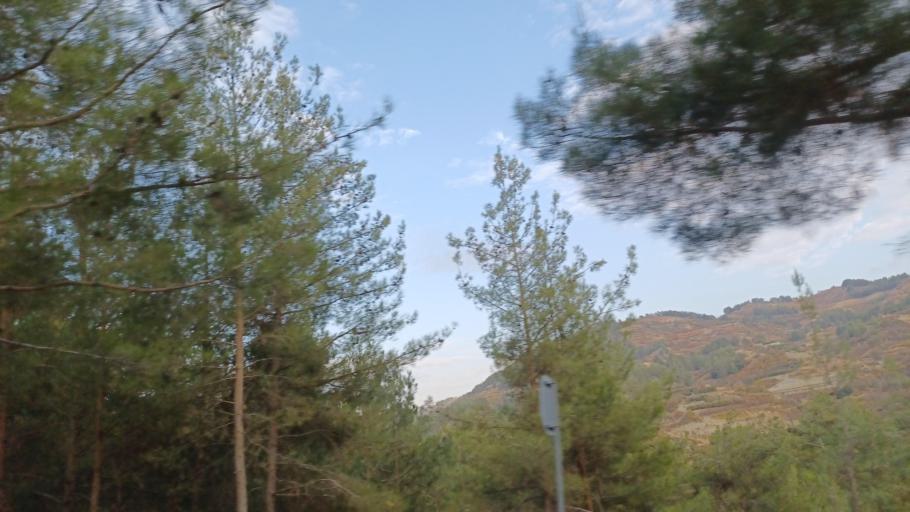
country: CY
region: Limassol
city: Kyperounta
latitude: 34.9380
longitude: 32.9321
